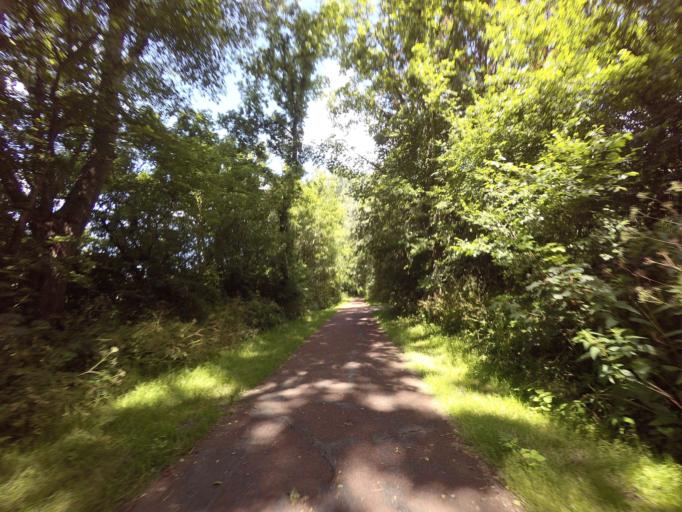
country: NL
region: North Holland
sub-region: Gemeente Den Helder
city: Den Helder
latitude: 52.9361
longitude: 4.7629
